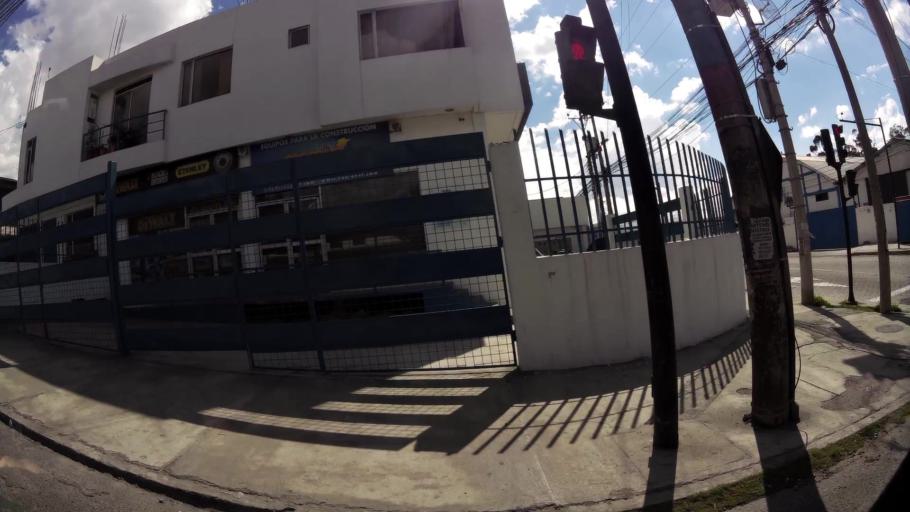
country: EC
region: Pichincha
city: Quito
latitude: -0.1124
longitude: -78.4744
